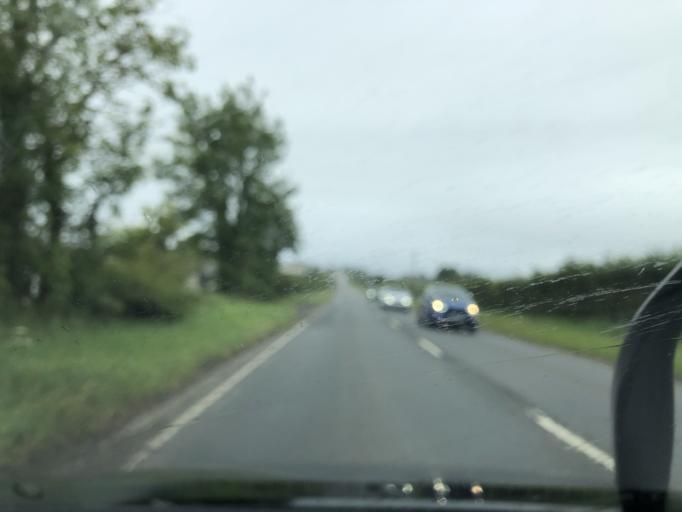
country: GB
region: Northern Ireland
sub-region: Down District
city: Dundrum
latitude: 54.2983
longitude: -5.8394
